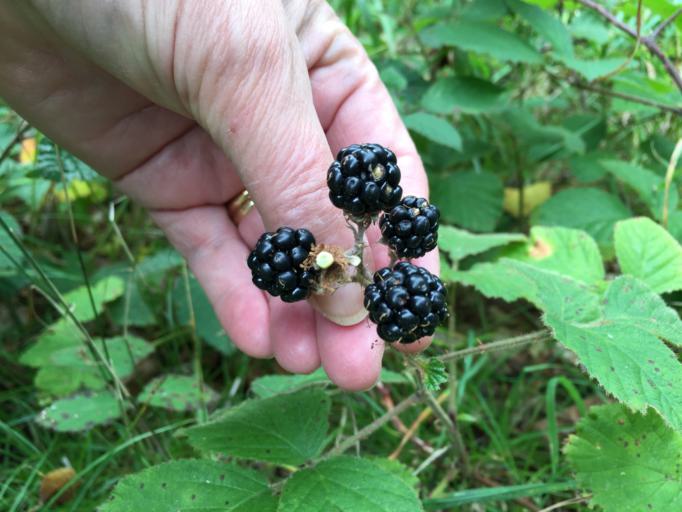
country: DK
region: South Denmark
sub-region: Sonderborg Kommune
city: Nordborg
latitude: 55.0141
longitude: 9.7565
